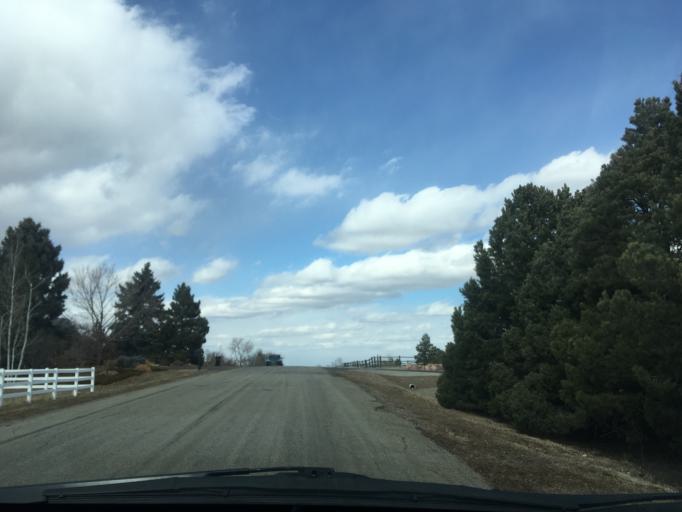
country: US
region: Colorado
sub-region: Boulder County
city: Lafayette
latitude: 39.9589
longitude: -105.0552
